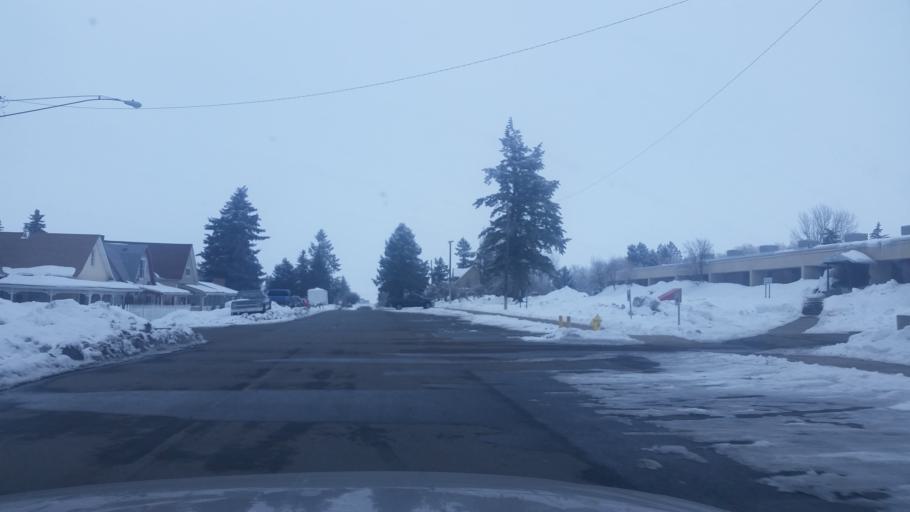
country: US
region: Washington
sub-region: Spokane County
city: Medical Lake
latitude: 47.6684
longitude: -117.8769
